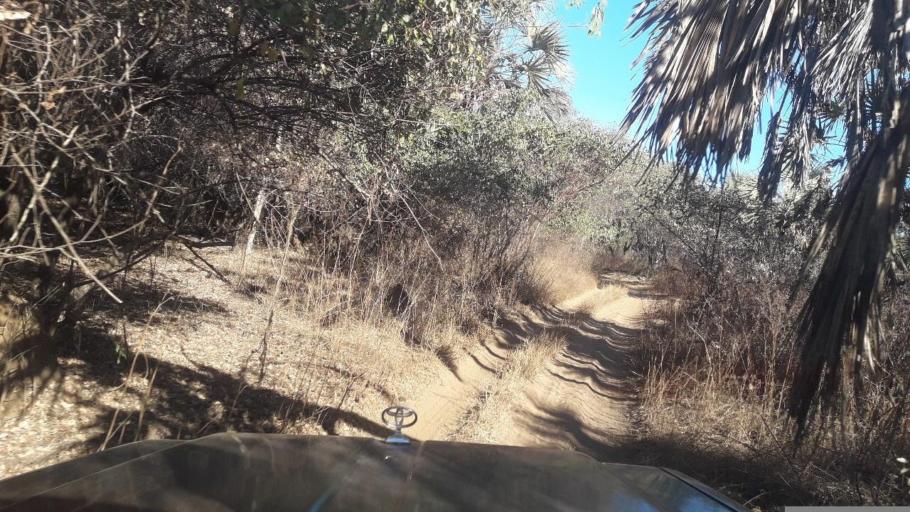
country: MG
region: Boeny
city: Sitampiky
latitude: -16.4084
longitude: 45.6007
